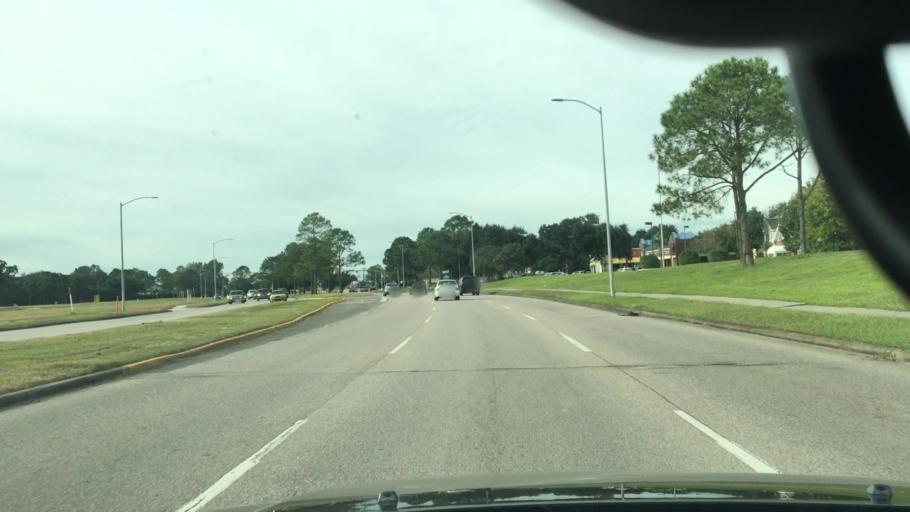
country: US
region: Texas
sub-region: Harris County
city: Webster
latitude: 29.5523
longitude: -95.1245
